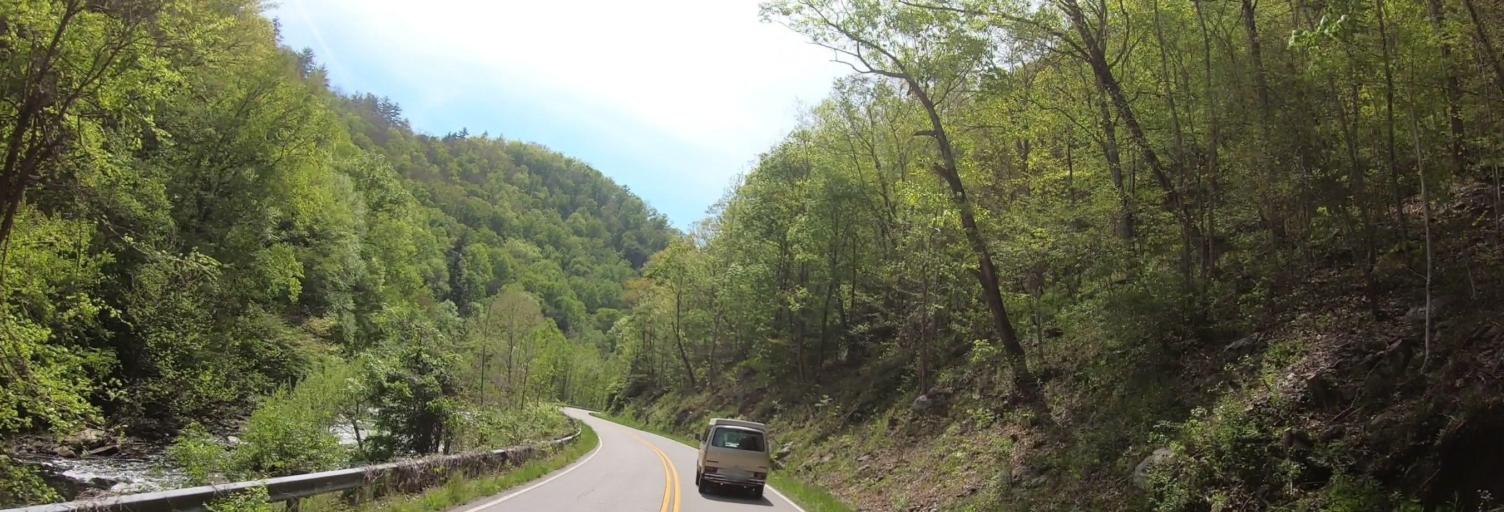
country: US
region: North Carolina
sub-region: Graham County
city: Robbinsville
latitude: 35.4378
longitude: -83.9203
